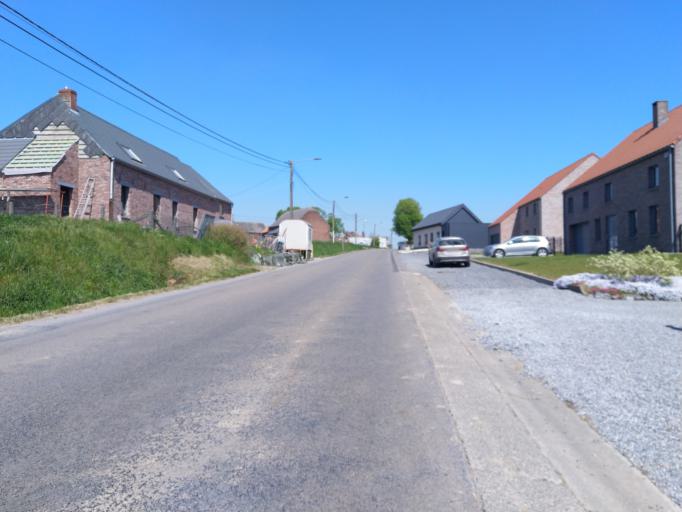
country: BE
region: Wallonia
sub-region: Province du Hainaut
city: Soignies
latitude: 50.5976
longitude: 4.0010
